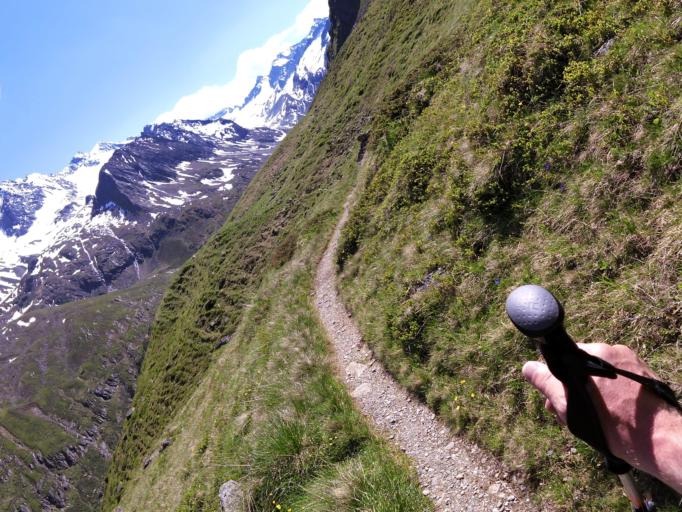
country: AT
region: Tyrol
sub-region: Politischer Bezirk Innsbruck Land
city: Gries im Sellrain
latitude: 47.0950
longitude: 11.1761
